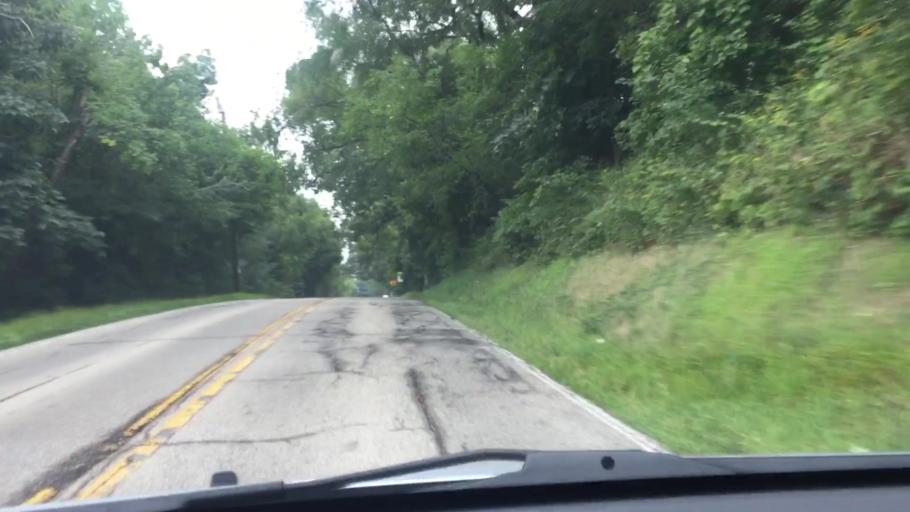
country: US
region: Wisconsin
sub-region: Waukesha County
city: Dousman
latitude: 43.0245
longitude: -88.4428
